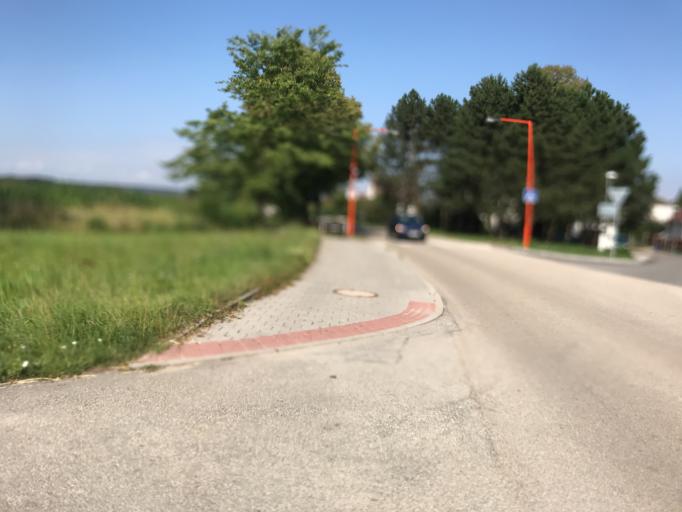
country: CZ
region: Jihocesky
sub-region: Okres Jindrichuv Hradec
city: Trebon
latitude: 49.0162
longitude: 14.7491
